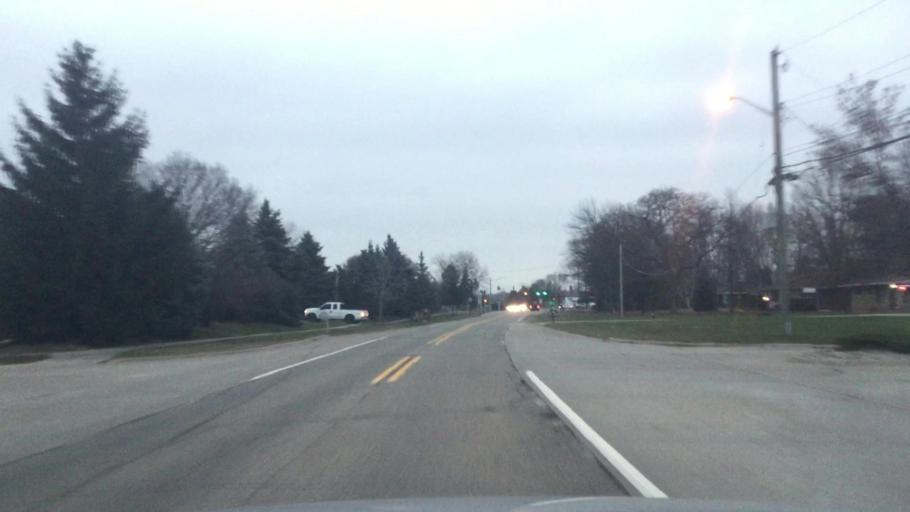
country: US
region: Michigan
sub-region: Macomb County
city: Fraser
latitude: 42.5818
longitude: -82.9738
